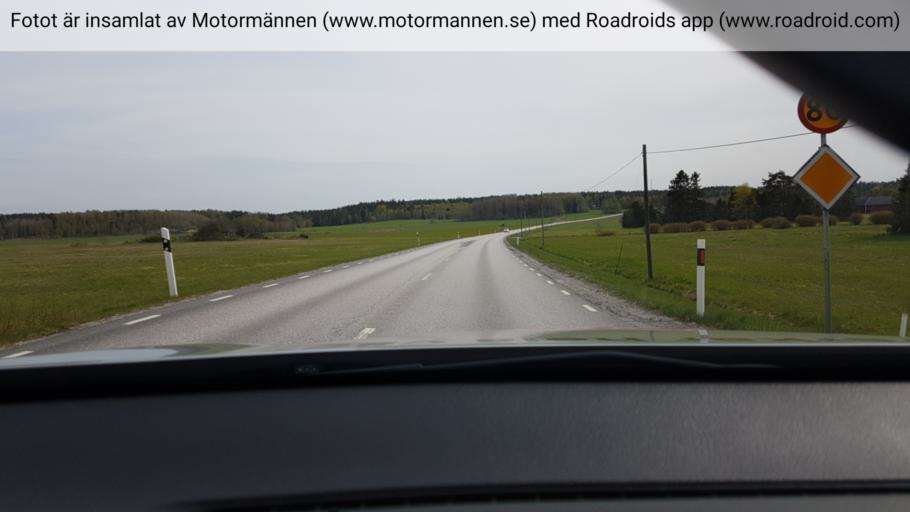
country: SE
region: Stockholm
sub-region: Vallentuna Kommun
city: Vallentuna
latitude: 59.7203
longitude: 18.0550
